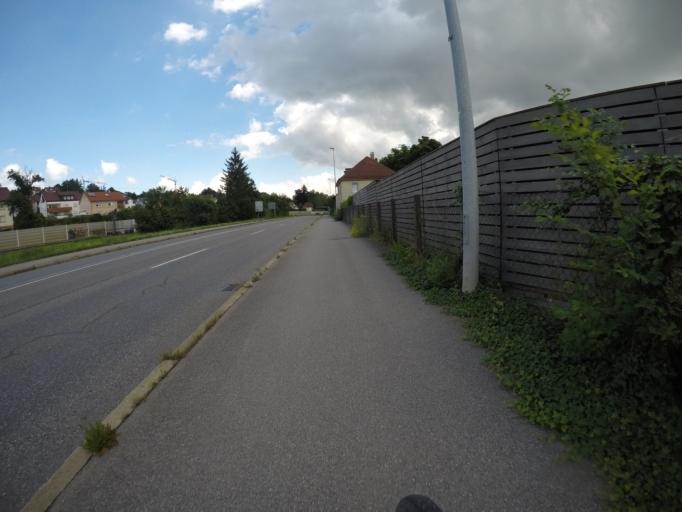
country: DE
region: Baden-Wuerttemberg
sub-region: Regierungsbezirk Stuttgart
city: Wangen
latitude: 48.7088
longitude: 9.6121
